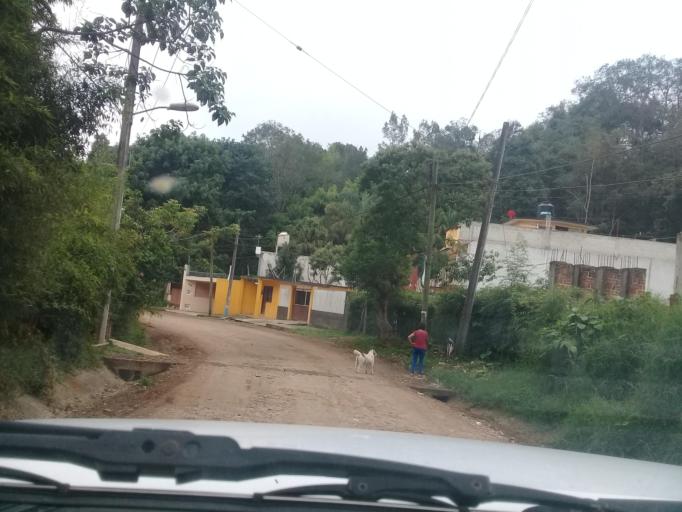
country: MX
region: Veracruz
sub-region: Xalapa
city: Lomas Verdes
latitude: 19.5065
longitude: -96.9084
